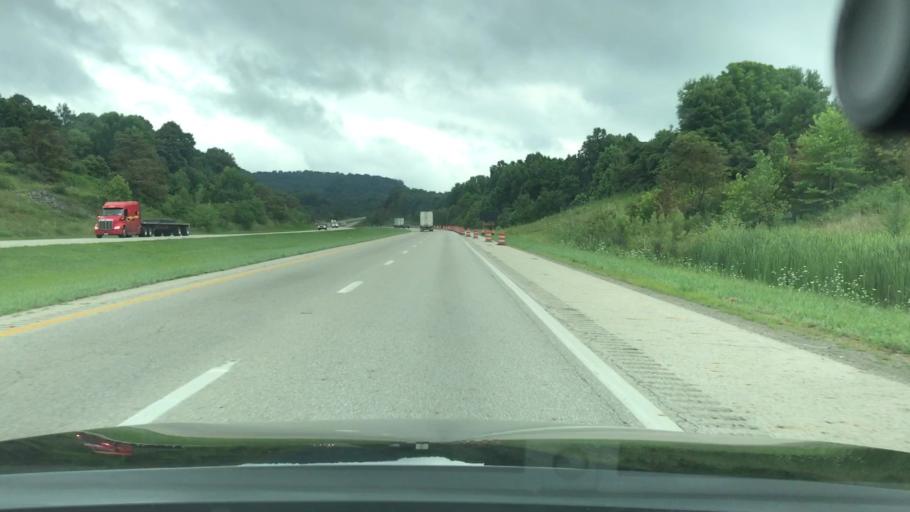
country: US
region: Ohio
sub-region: Ross County
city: Chillicothe
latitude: 39.2472
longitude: -82.8473
